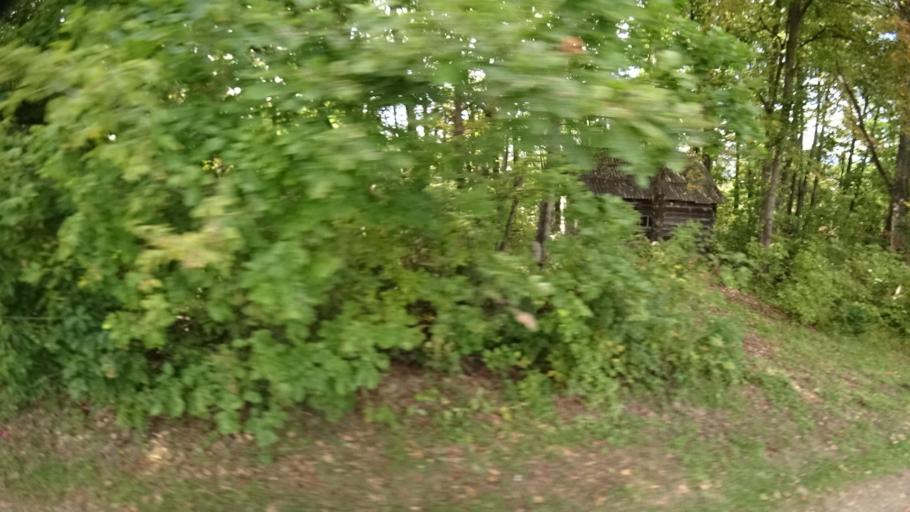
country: RU
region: Primorskiy
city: Dostoyevka
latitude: 44.3227
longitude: 133.4851
